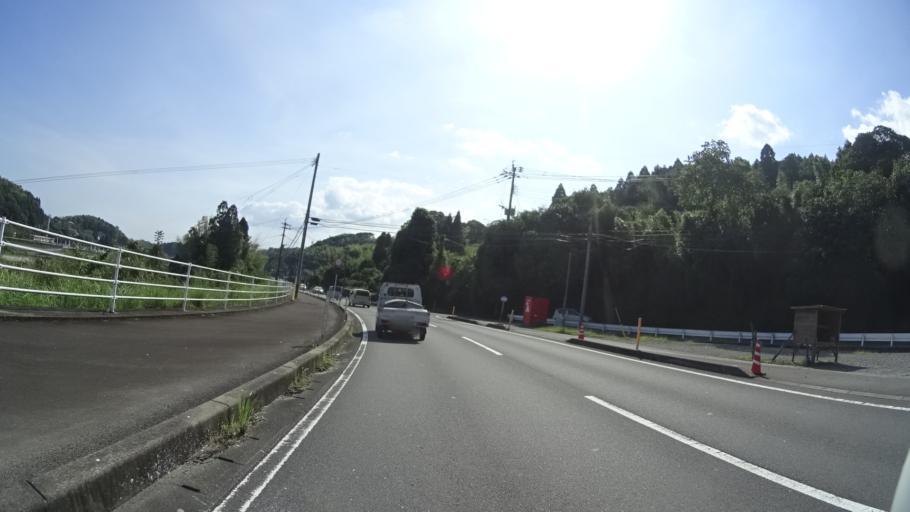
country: JP
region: Kagoshima
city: Kagoshima-shi
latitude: 31.6627
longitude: 130.5523
